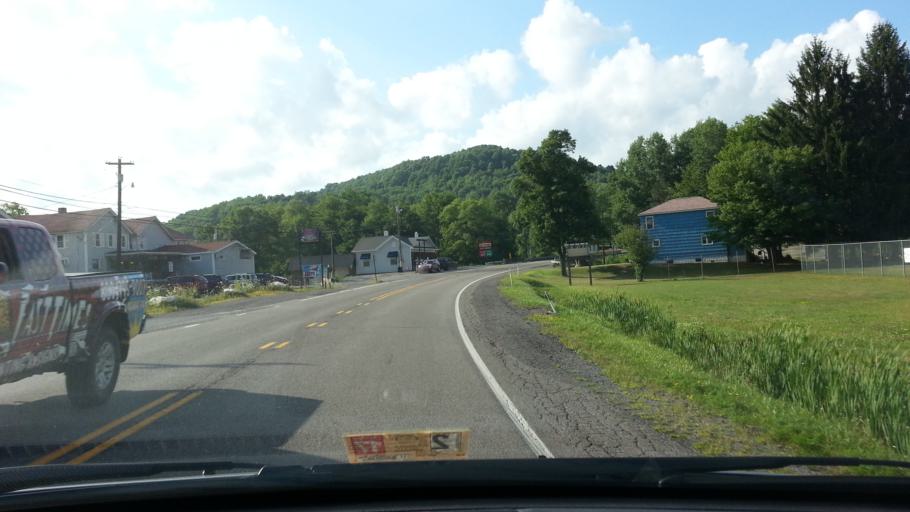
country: US
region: Pennsylvania
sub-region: Elk County
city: Saint Marys
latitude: 41.2904
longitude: -78.5040
